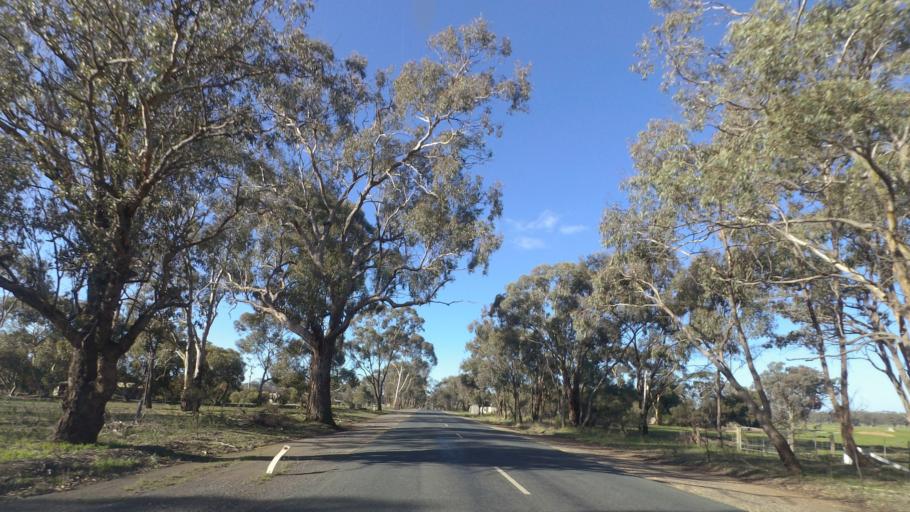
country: AU
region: Victoria
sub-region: Greater Bendigo
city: Epsom
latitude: -36.6626
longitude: 144.4523
